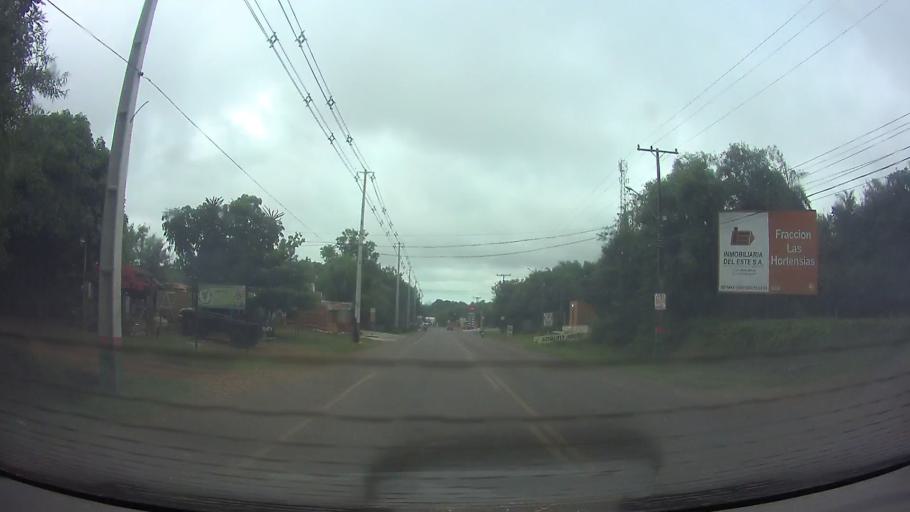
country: PY
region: Cordillera
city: Altos
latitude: -25.2699
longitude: -57.2547
